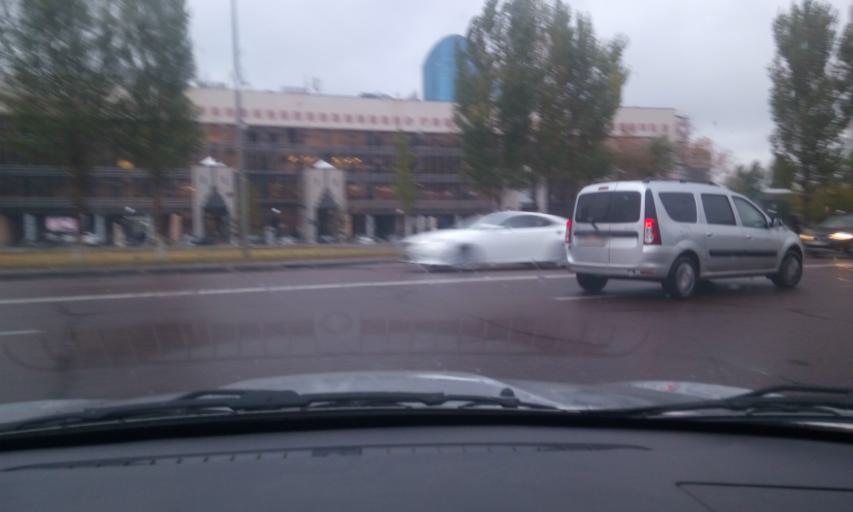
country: KZ
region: Astana Qalasy
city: Astana
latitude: 51.1346
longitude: 71.4146
